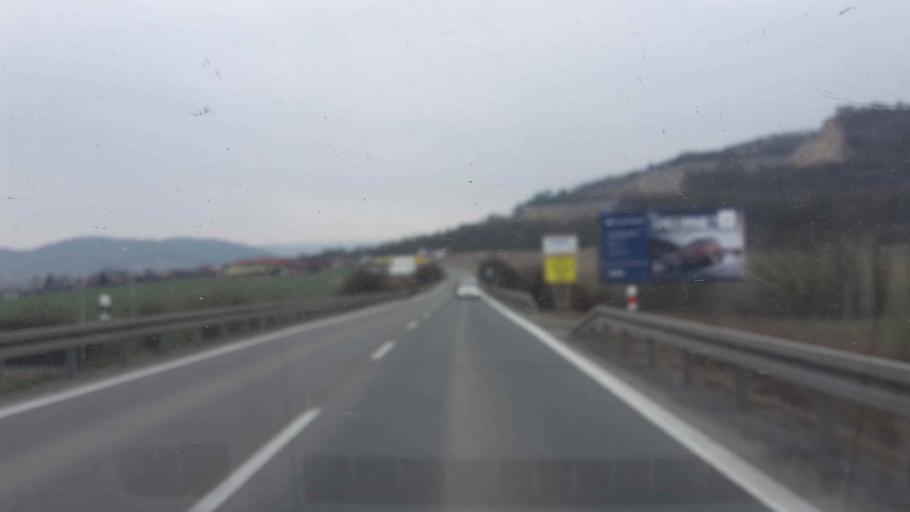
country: CZ
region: South Moravian
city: Cebin
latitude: 49.3108
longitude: 16.4909
